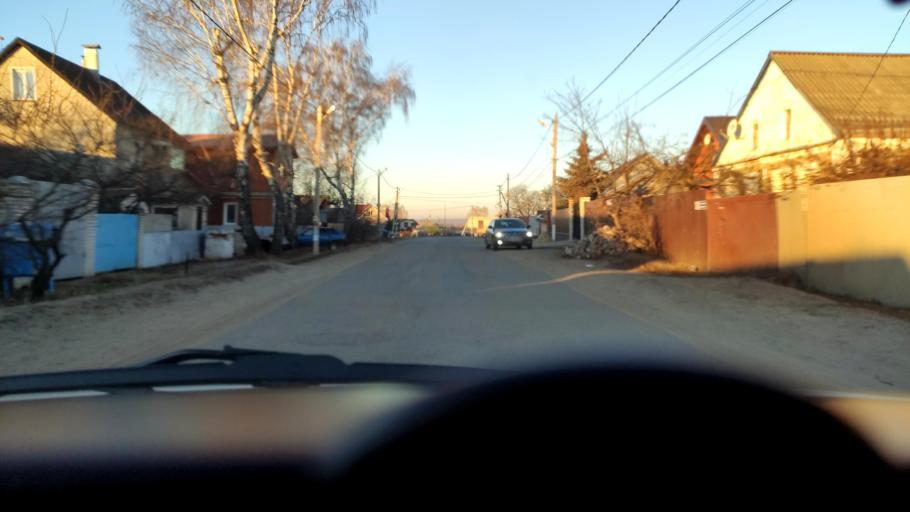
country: RU
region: Voronezj
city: Podgornoye
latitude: 51.7396
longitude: 39.1511
